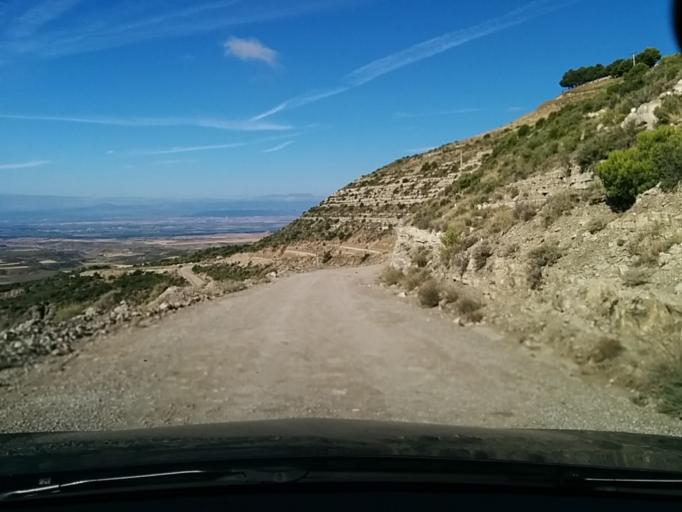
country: ES
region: Aragon
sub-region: Provincia de Zaragoza
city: Novillas
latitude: 42.0210
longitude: -1.3194
